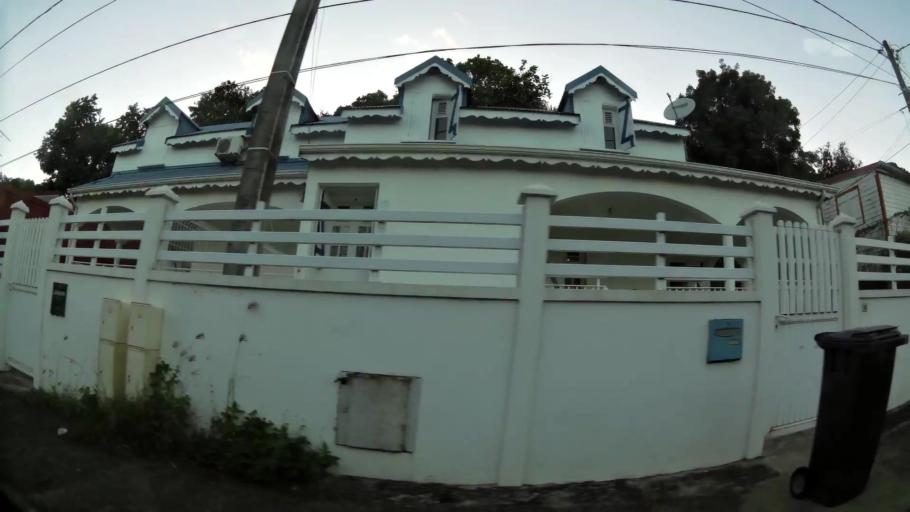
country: GP
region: Guadeloupe
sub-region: Guadeloupe
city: Les Abymes
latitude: 16.2652
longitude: -61.5007
